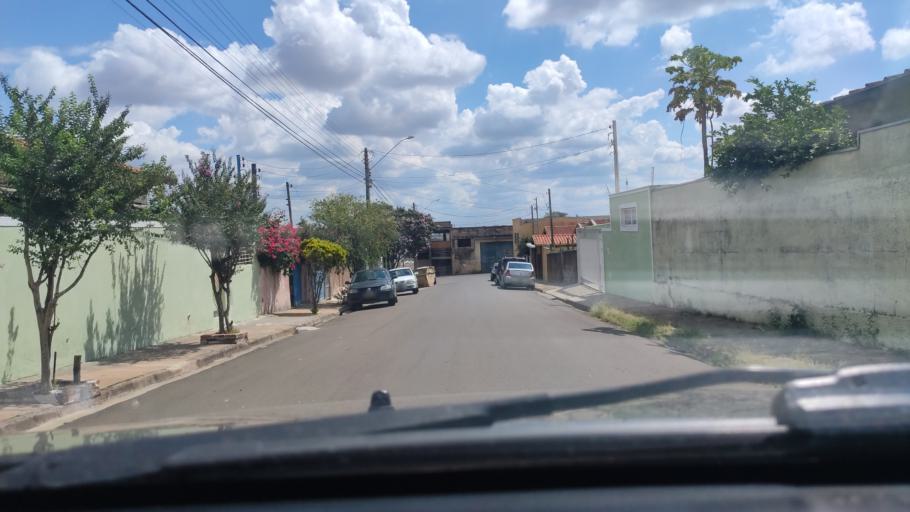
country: BR
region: Sao Paulo
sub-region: Sao Carlos
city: Sao Carlos
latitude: -22.0084
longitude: -47.8717
